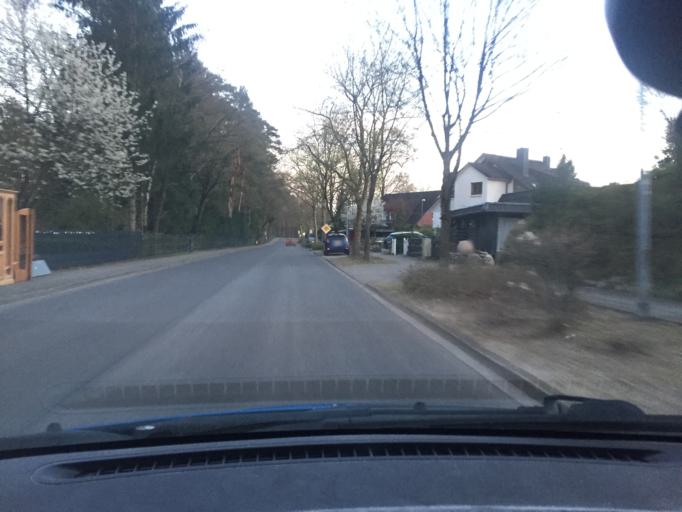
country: DE
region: Lower Saxony
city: Buchholz in der Nordheide
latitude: 53.3130
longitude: 9.8645
